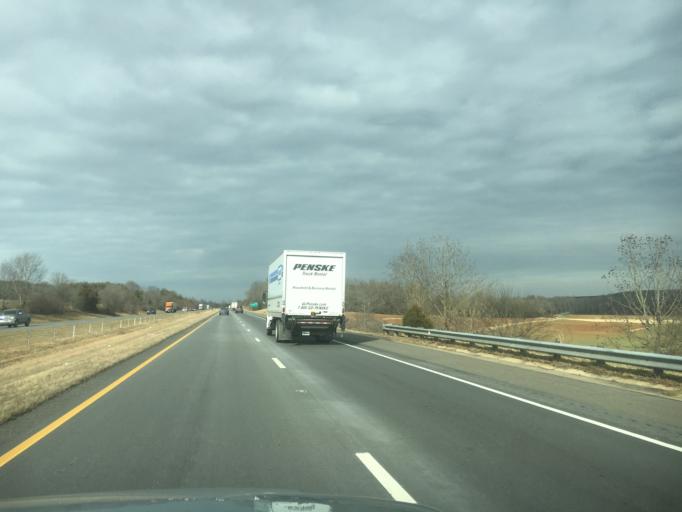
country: US
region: North Carolina
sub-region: Catawba County
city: Maiden
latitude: 35.5735
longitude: -81.2473
